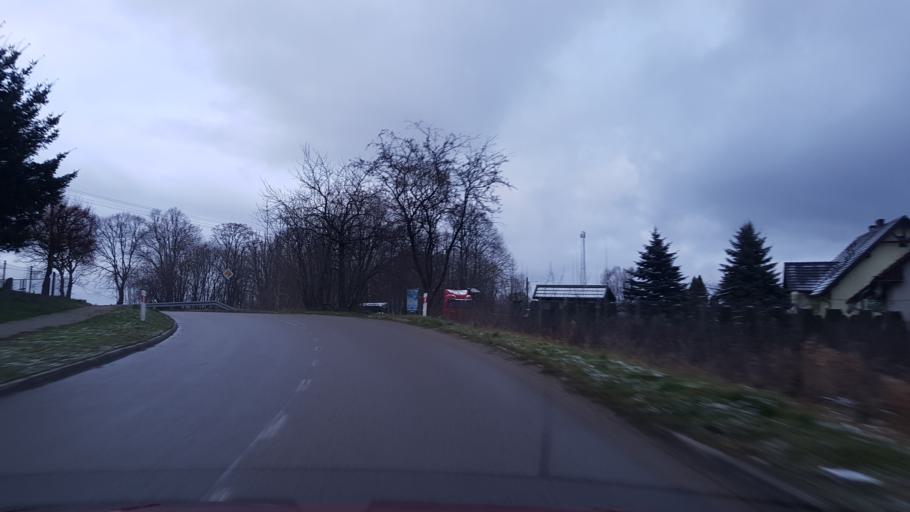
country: PL
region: Pomeranian Voivodeship
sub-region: Powiat bytowski
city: Tuchomie
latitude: 54.1193
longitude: 17.3372
